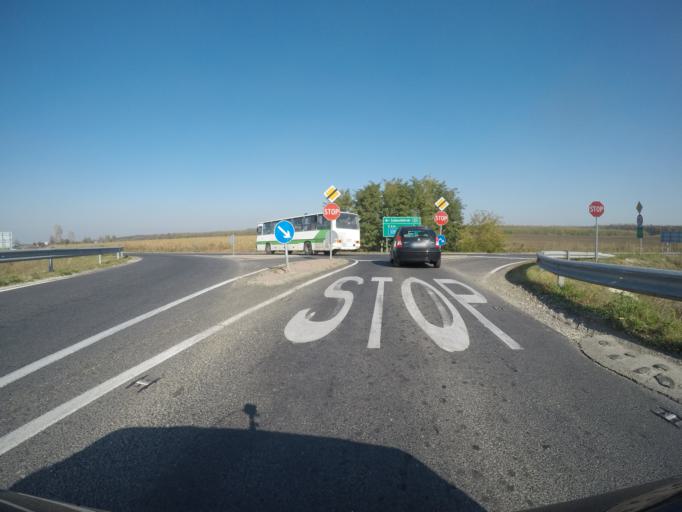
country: HU
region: Tolna
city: Szedres
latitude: 46.4967
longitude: 18.6731
